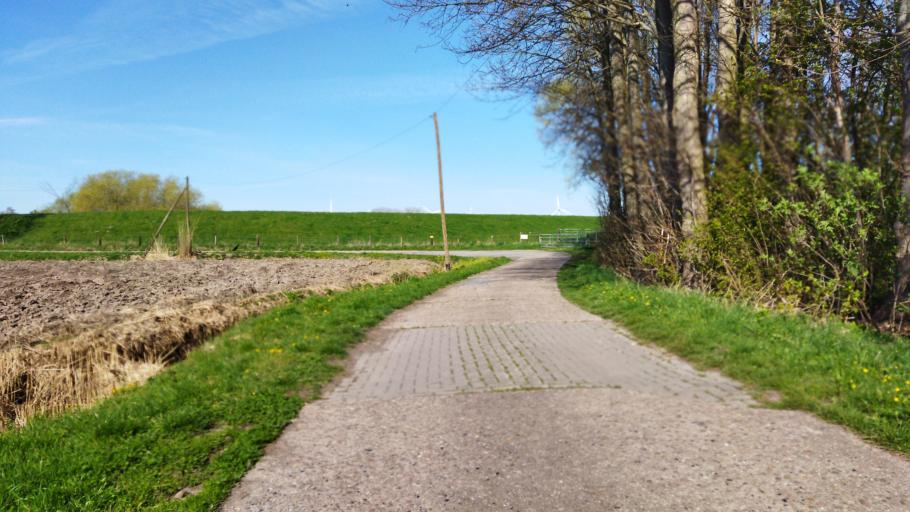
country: DE
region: Lower Saxony
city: Elsfleth
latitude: 53.2054
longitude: 8.4567
